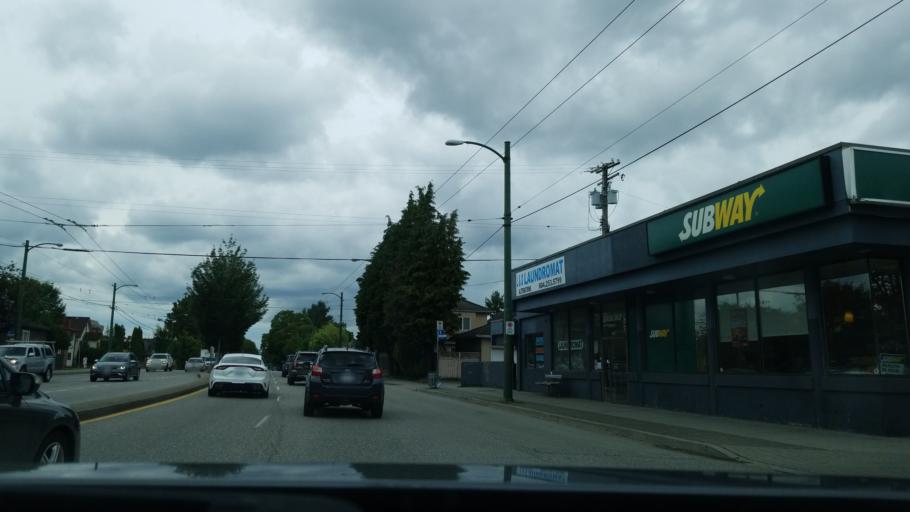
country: CA
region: British Columbia
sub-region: Fraser Valley Regional District
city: North Vancouver
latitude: 49.2622
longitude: -123.0569
